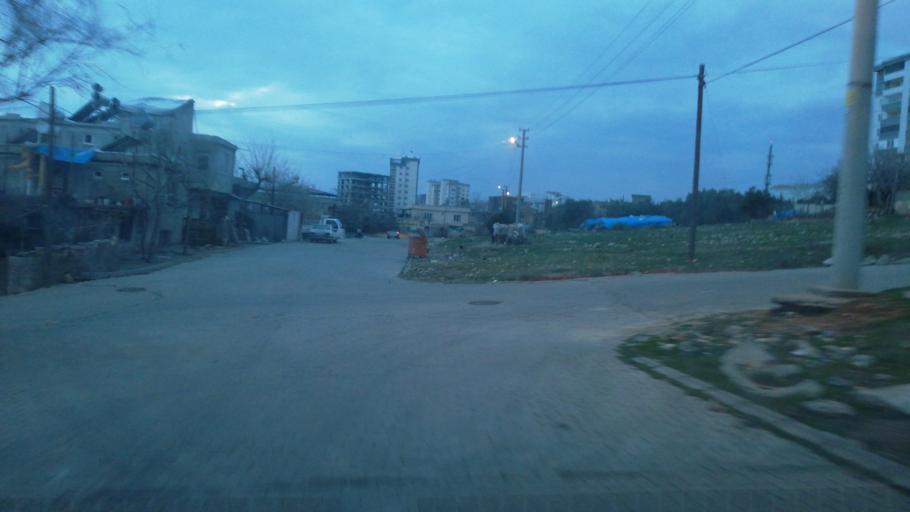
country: TR
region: Kahramanmaras
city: Kahramanmaras
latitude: 37.5983
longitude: 36.8356
